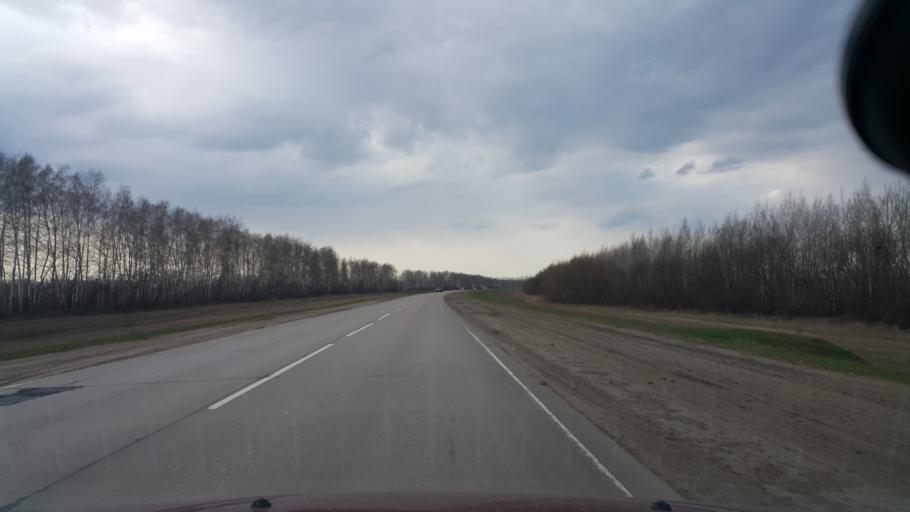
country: RU
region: Tambov
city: Znamenka
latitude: 52.4086
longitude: 41.3839
